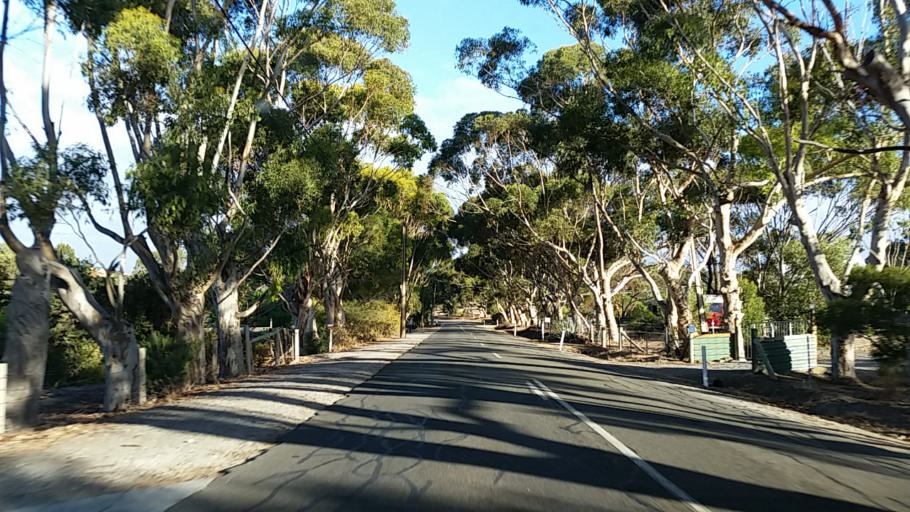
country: AU
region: South Australia
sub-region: Yankalilla
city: Normanville
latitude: -35.5236
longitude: 138.2244
